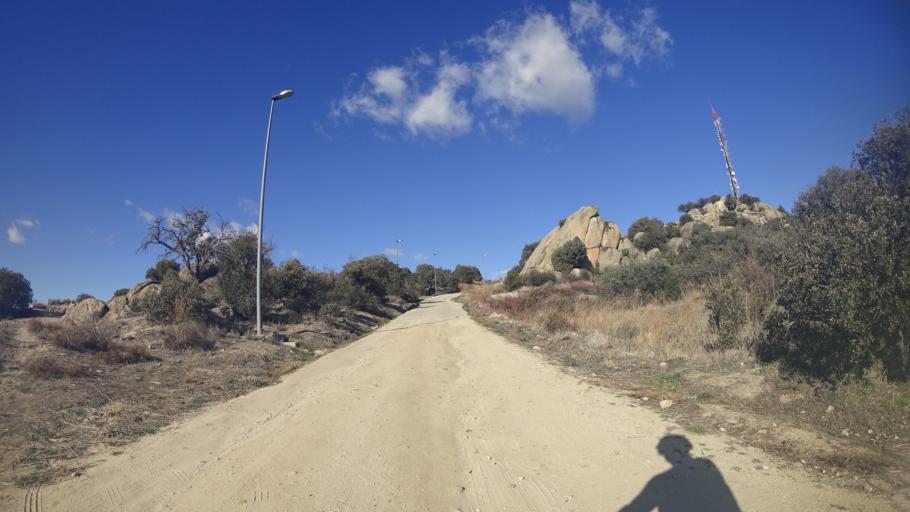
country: ES
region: Madrid
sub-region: Provincia de Madrid
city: Torrelodones
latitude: 40.5808
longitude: -3.9399
